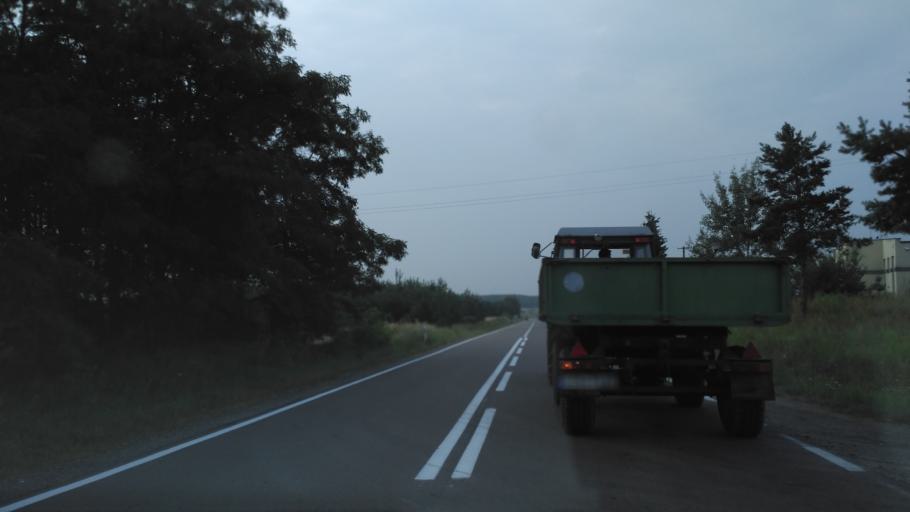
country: PL
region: Lublin Voivodeship
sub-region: Powiat chelmski
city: Rejowiec Fabryczny
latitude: 51.1802
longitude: 23.1756
